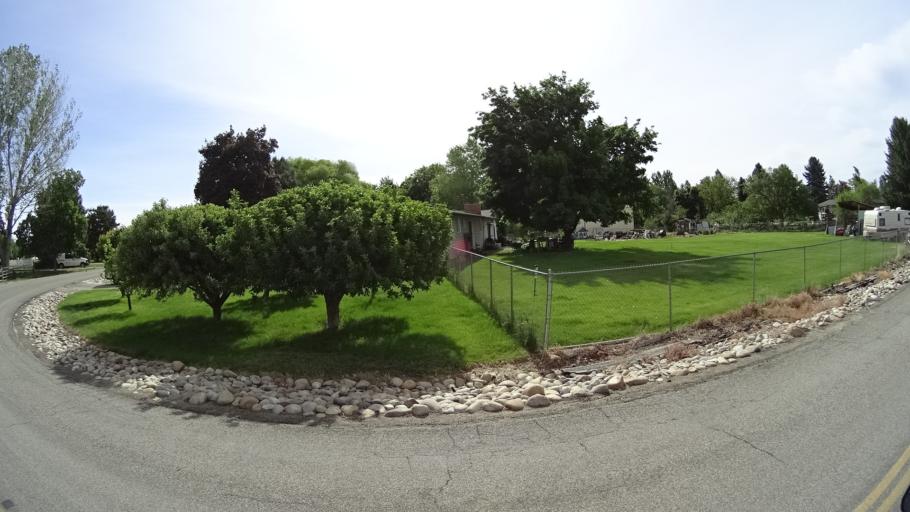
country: US
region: Idaho
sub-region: Ada County
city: Garden City
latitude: 43.5667
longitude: -116.3021
